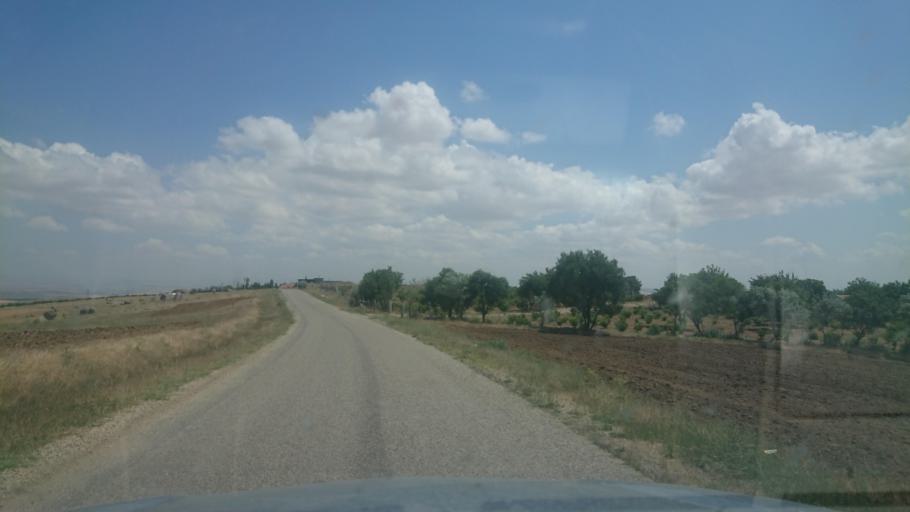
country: TR
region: Aksaray
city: Agacoren
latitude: 38.8707
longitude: 33.9400
